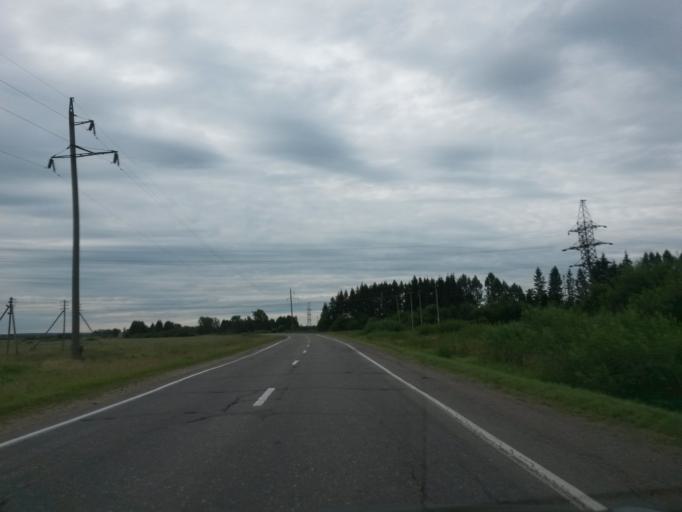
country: RU
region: Jaroslavl
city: Gavrilov-Yam
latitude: 57.3478
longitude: 39.7910
